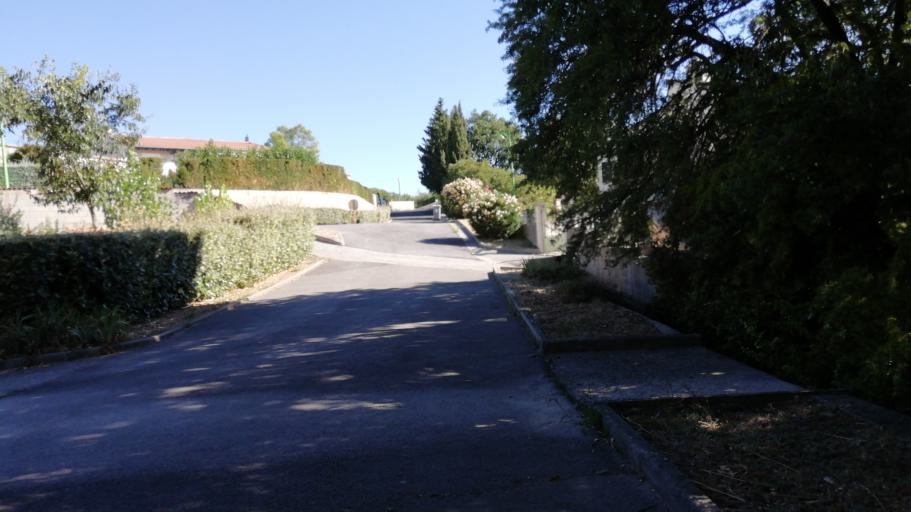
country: FR
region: Languedoc-Roussillon
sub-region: Departement de l'Herault
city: Saint-Martin-de-Londres
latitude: 43.7888
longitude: 3.7284
